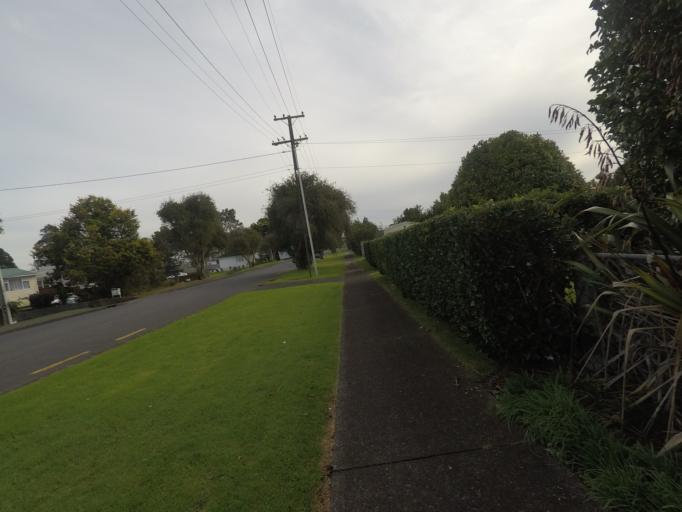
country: NZ
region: Auckland
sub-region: Auckland
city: Mangere
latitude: -36.9471
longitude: 174.8128
